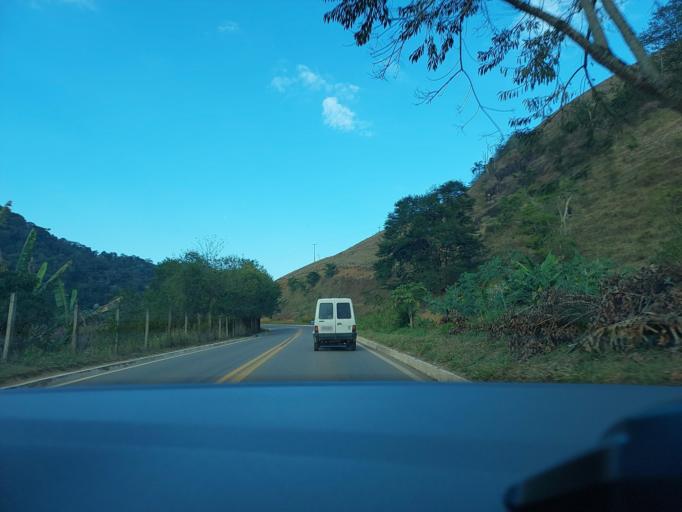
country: BR
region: Minas Gerais
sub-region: Muriae
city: Muriae
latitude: -21.0753
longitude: -42.5023
